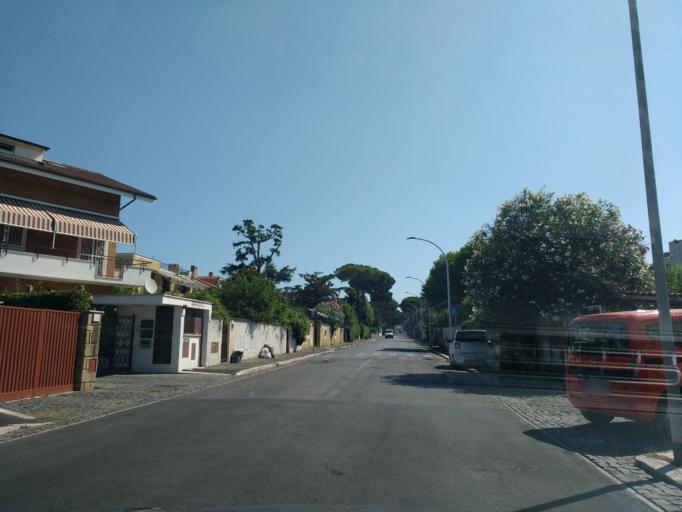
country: IT
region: Latium
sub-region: Citta metropolitana di Roma Capitale
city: Acilia-Castel Fusano-Ostia Antica
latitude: 41.7662
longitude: 12.3634
